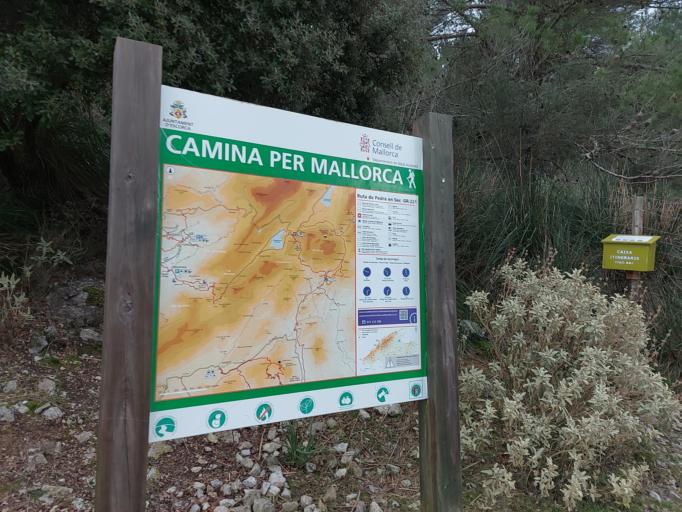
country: ES
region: Balearic Islands
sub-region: Illes Balears
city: Fornalutx
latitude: 39.7870
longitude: 2.7992
